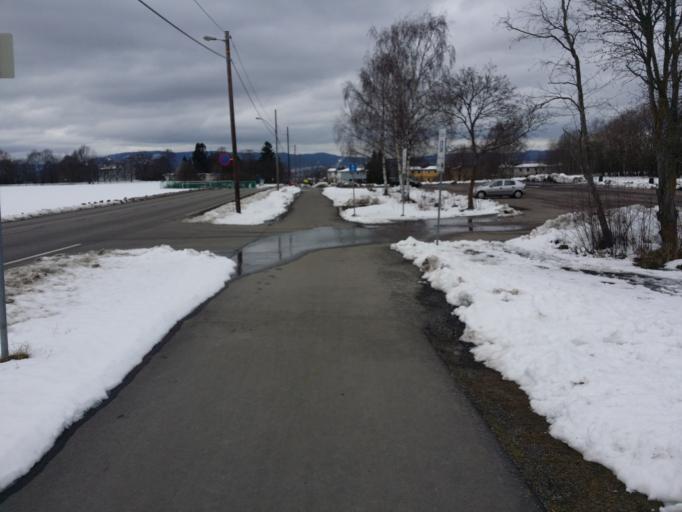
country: NO
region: Oslo
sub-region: Oslo
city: Oslo
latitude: 59.8958
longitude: 10.7773
